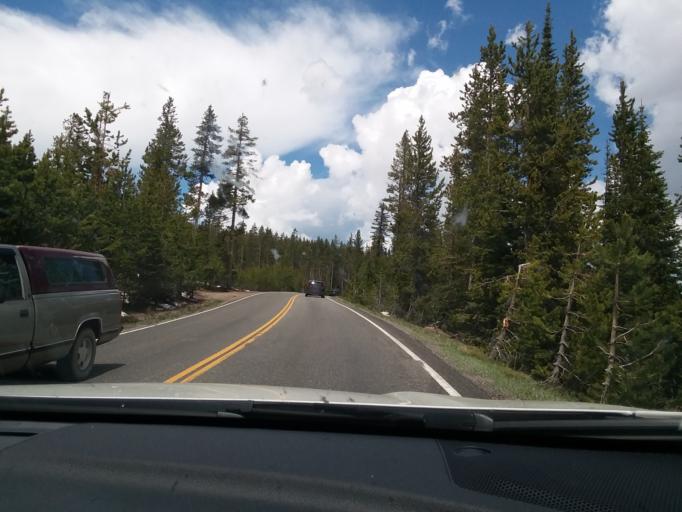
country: US
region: Montana
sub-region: Gallatin County
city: West Yellowstone
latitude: 44.1991
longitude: -110.6589
